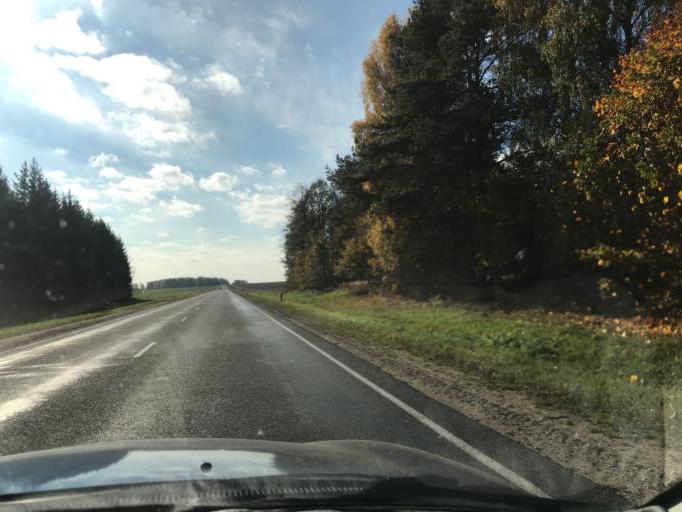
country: BY
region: Grodnenskaya
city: Voranava
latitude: 54.2024
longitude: 25.3484
